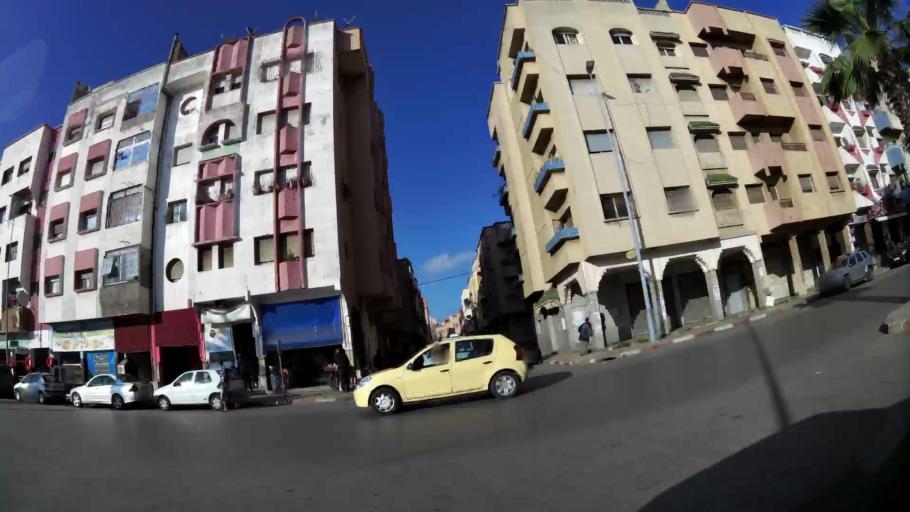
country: MA
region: Rabat-Sale-Zemmour-Zaer
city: Sale
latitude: 34.0532
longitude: -6.7924
